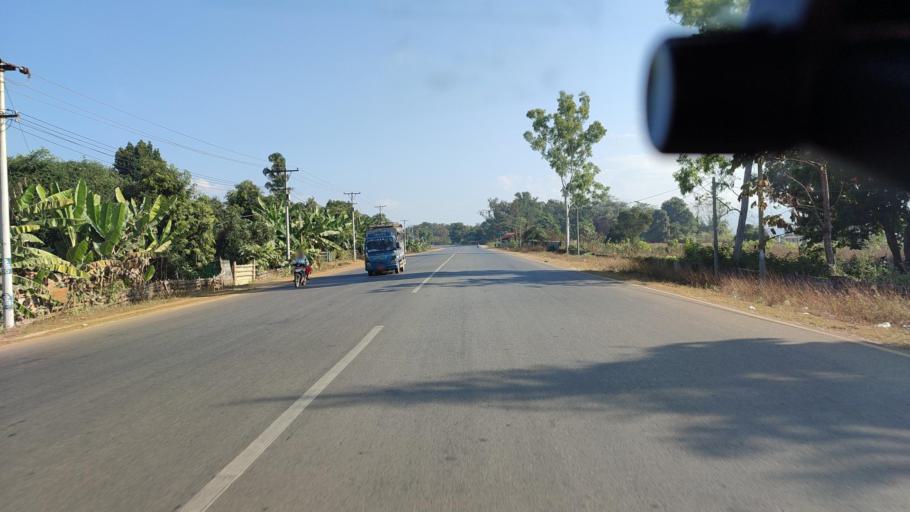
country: MM
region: Shan
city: Lashio
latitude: 23.2392
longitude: 97.9153
